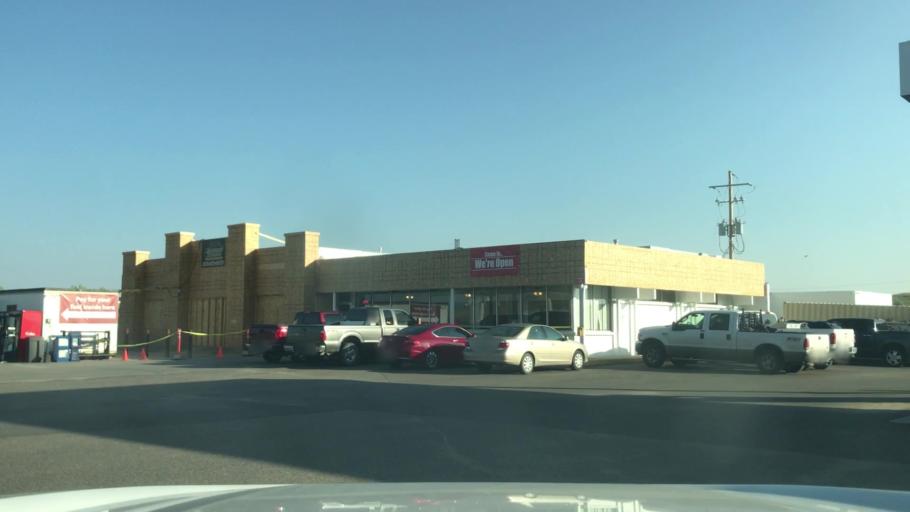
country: US
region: Wyoming
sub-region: Converse County
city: Douglas
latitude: 42.7378
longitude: -105.3463
